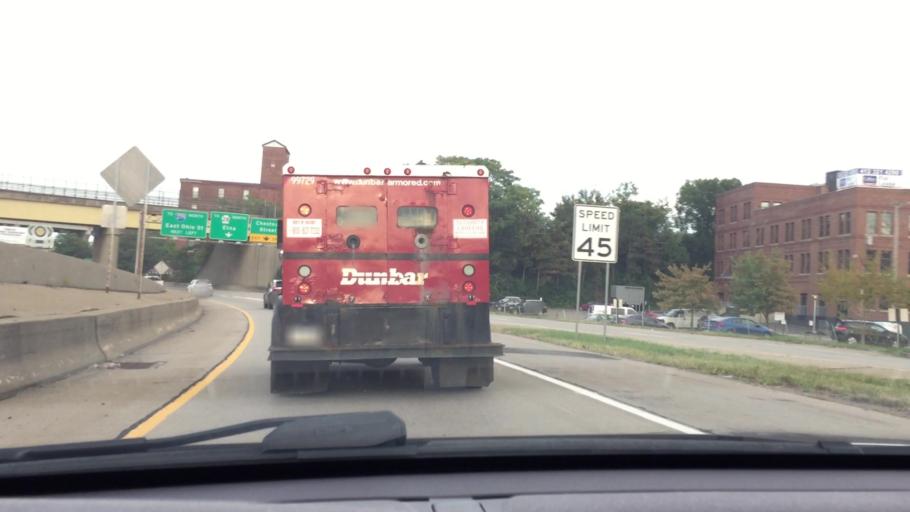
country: US
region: Pennsylvania
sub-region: Allegheny County
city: Pittsburgh
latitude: 40.4496
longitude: -79.9989
